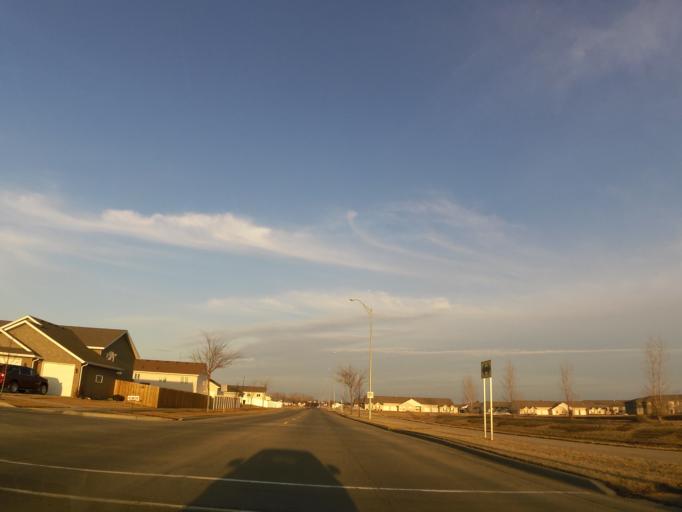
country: US
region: North Dakota
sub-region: Grand Forks County
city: Grand Forks
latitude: 47.8823
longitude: -97.0537
